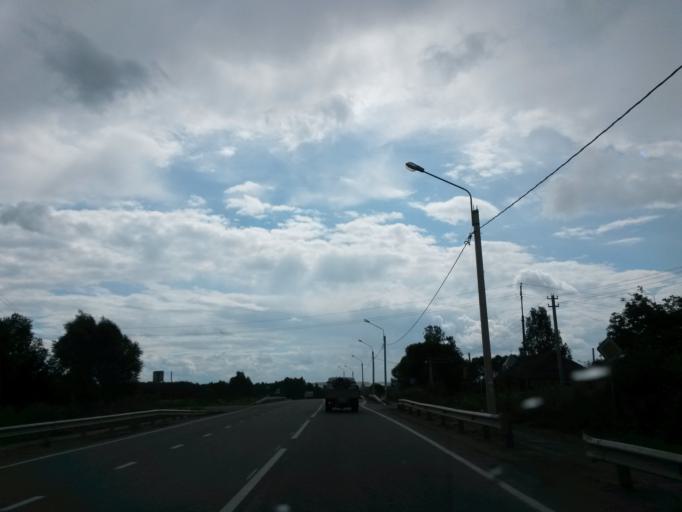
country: RU
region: Jaroslavl
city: Gavrilov-Yam
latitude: 57.3484
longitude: 39.9092
